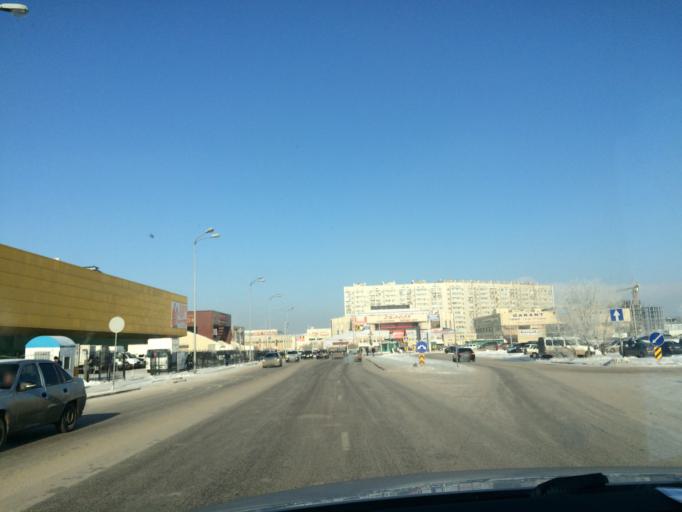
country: KZ
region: Astana Qalasy
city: Astana
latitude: 51.1772
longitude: 71.4371
